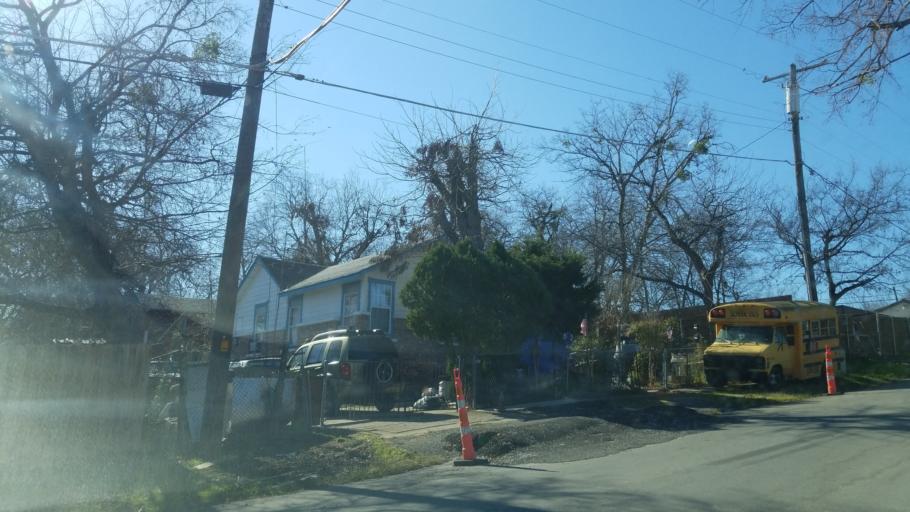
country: US
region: Texas
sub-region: Dallas County
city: Cockrell Hill
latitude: 32.7527
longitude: -96.9079
